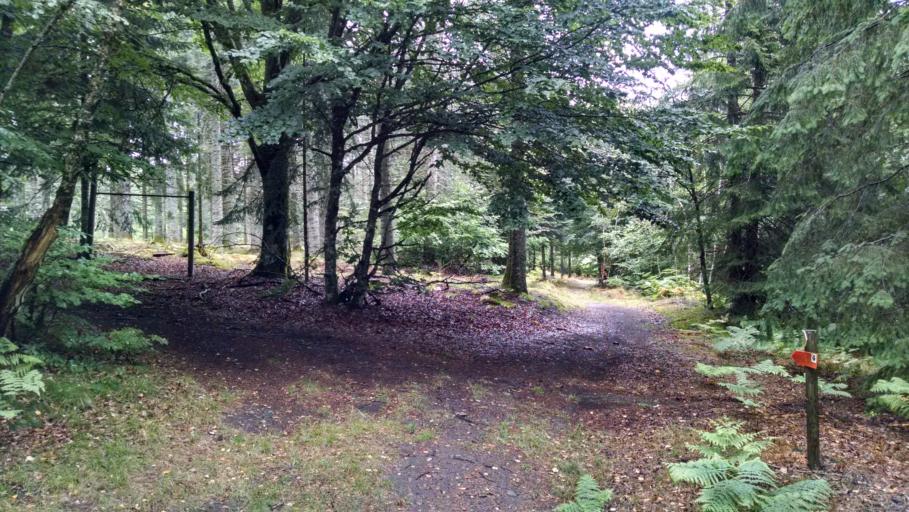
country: FR
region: Limousin
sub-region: Departement de la Creuse
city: La Courtine
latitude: 45.6975
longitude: 2.1225
